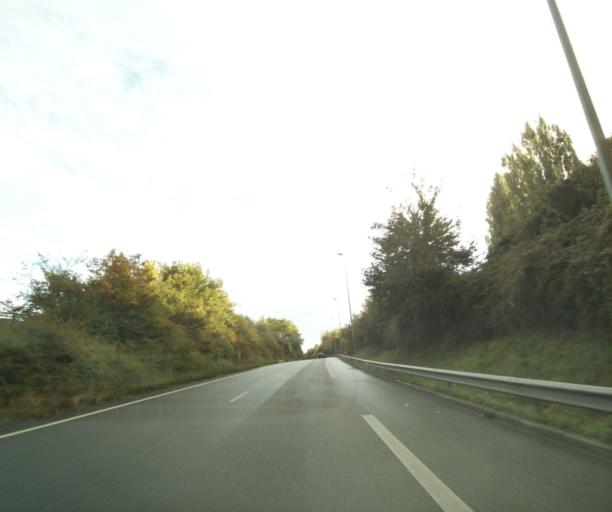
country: FR
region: Nord-Pas-de-Calais
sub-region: Departement du Nord
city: Wasquehal
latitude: 50.6705
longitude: 3.1141
